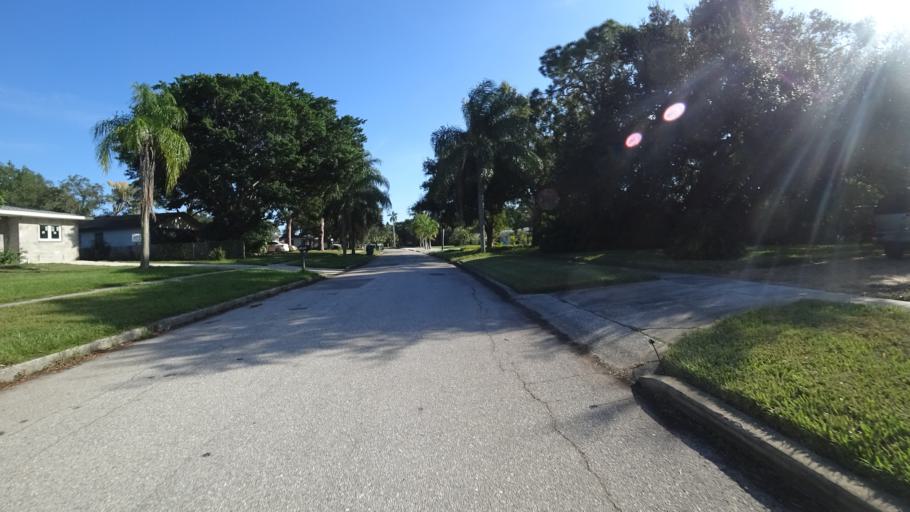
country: US
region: Florida
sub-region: Manatee County
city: West Bradenton
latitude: 27.4886
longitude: -82.6398
